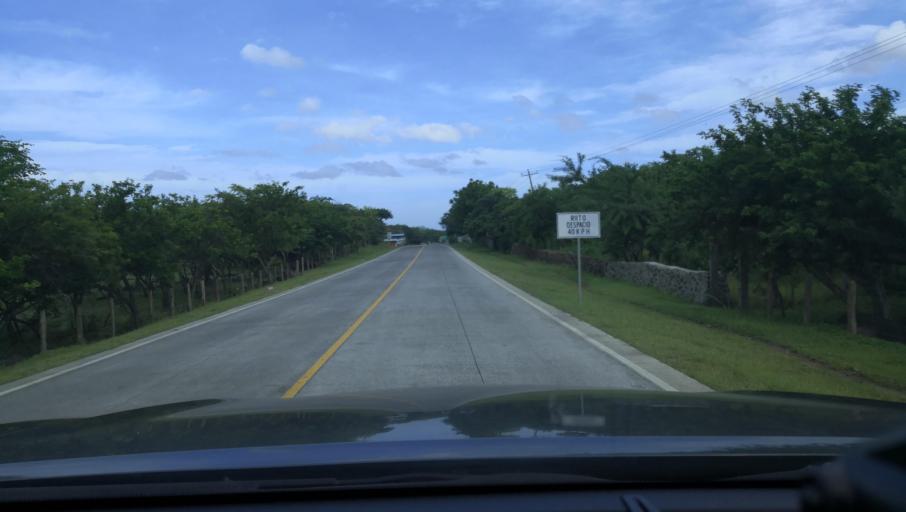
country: NI
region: Boaco
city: San Lorenzo
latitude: 12.1887
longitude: -85.7079
